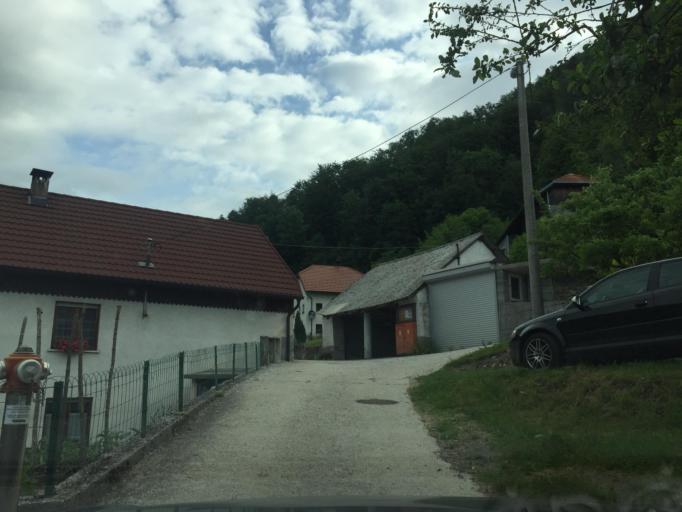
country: SI
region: Tolmin
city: Tolmin
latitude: 46.1682
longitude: 13.8379
